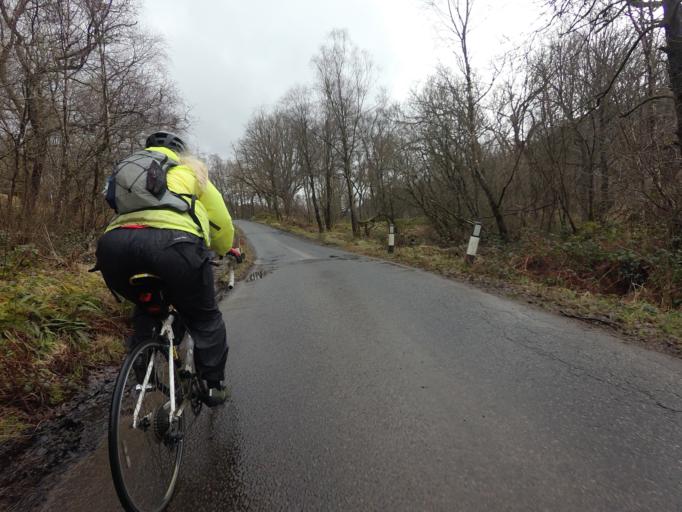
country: GB
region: Scotland
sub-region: West Dunbartonshire
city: Balloch
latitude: 56.2205
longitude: -4.5494
